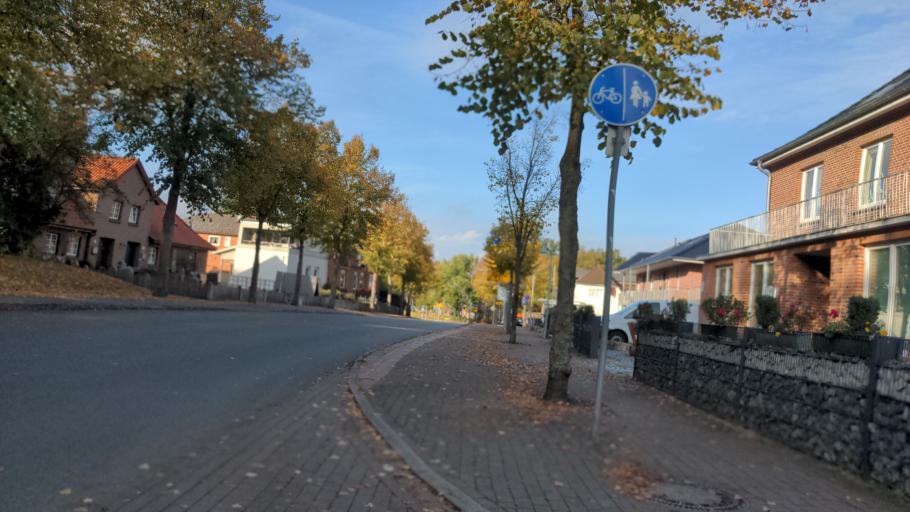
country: DE
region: Schleswig-Holstein
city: Lensahn
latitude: 54.2181
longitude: 10.8833
